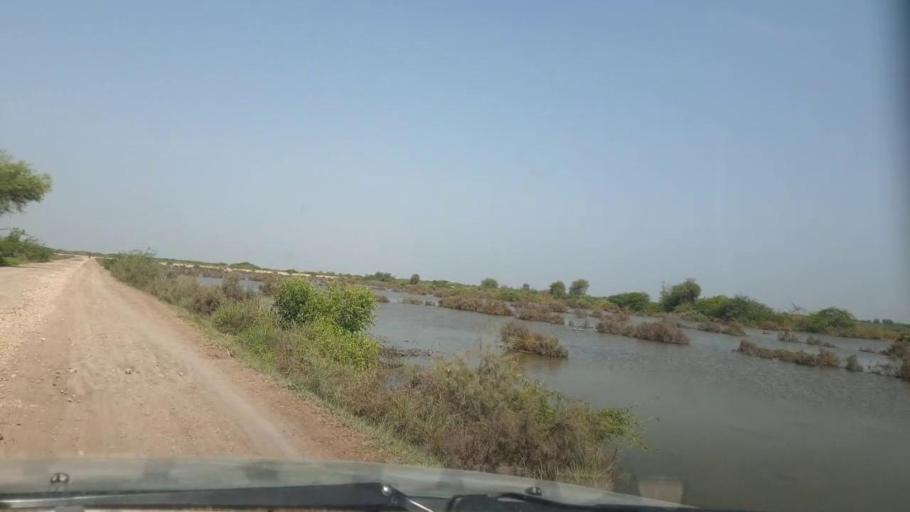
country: PK
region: Sindh
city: Tando Ghulam Ali
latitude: 25.1111
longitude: 68.8021
